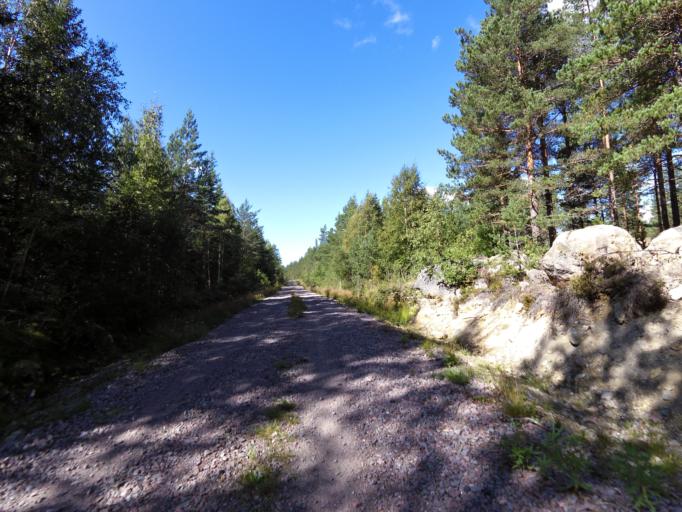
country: SE
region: Gaevleborg
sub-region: Gavle Kommun
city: Valbo
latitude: 60.7290
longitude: 16.9977
